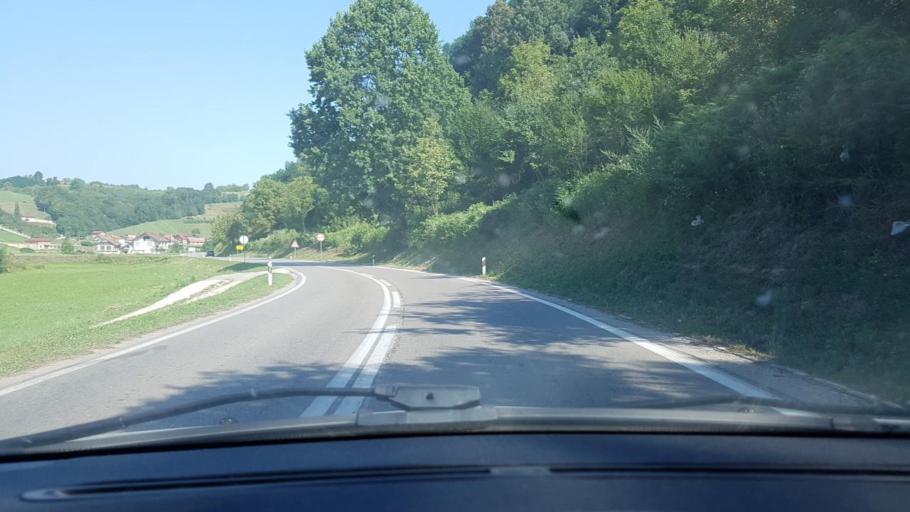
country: BA
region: Federation of Bosnia and Herzegovina
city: Sumatac
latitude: 45.1057
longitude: 15.8694
